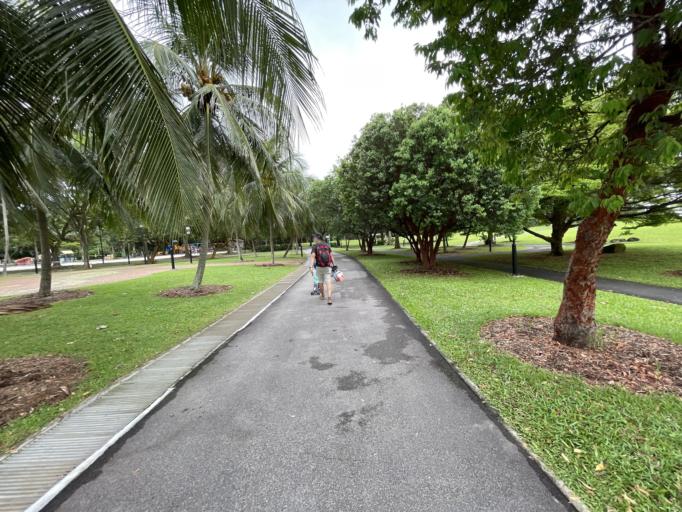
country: SG
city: Singapore
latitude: 1.2969
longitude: 103.7616
